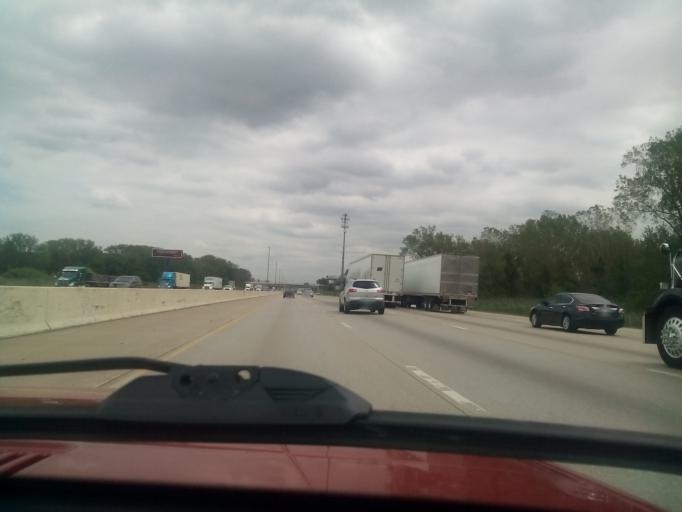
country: US
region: Indiana
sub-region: Lake County
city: Gary
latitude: 41.5697
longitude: -87.3832
